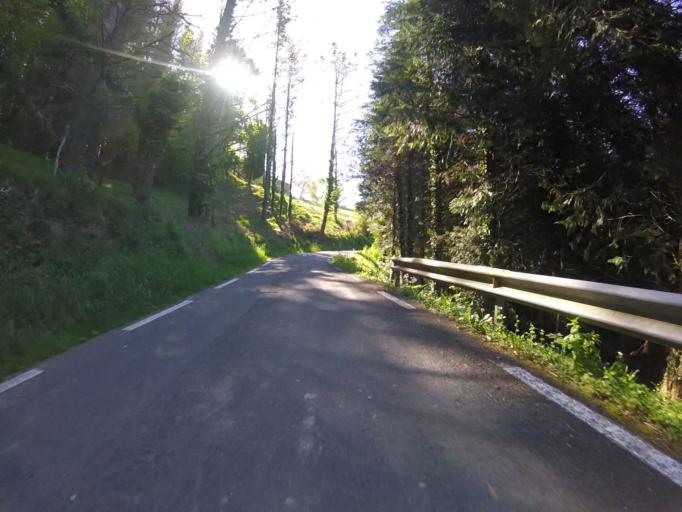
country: ES
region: Basque Country
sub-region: Provincia de Guipuzcoa
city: Aizarnazabal
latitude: 43.2285
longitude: -2.2147
